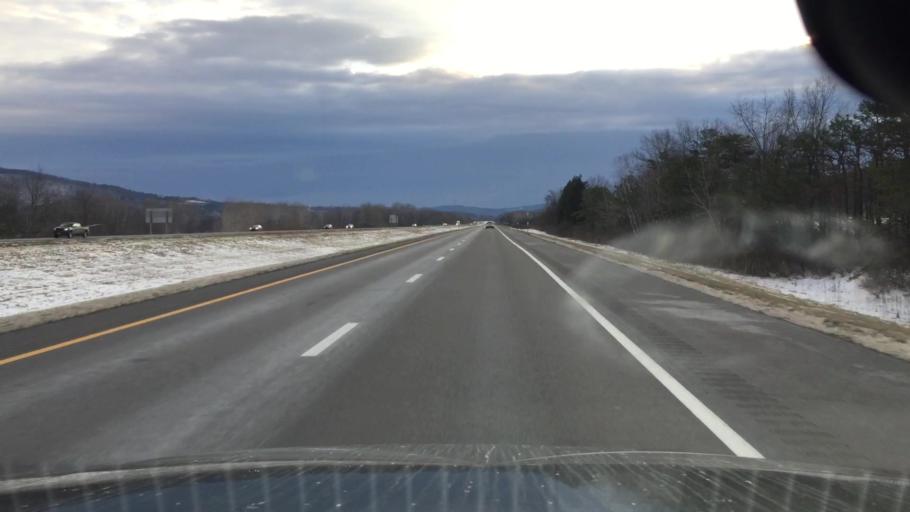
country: US
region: Pennsylvania
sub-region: Bradford County
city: South Waverly
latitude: 42.0009
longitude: -76.6127
